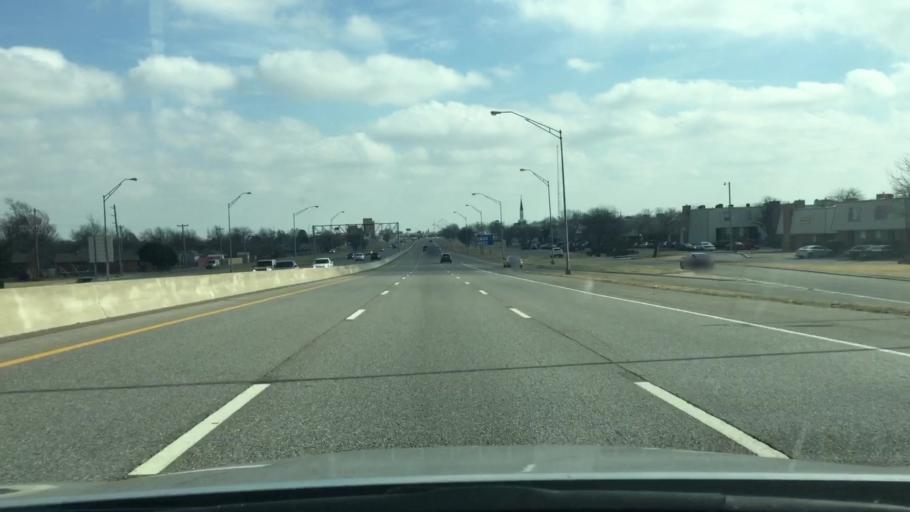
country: US
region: Oklahoma
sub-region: Oklahoma County
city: Oklahoma City
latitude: 35.3935
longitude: -97.5633
